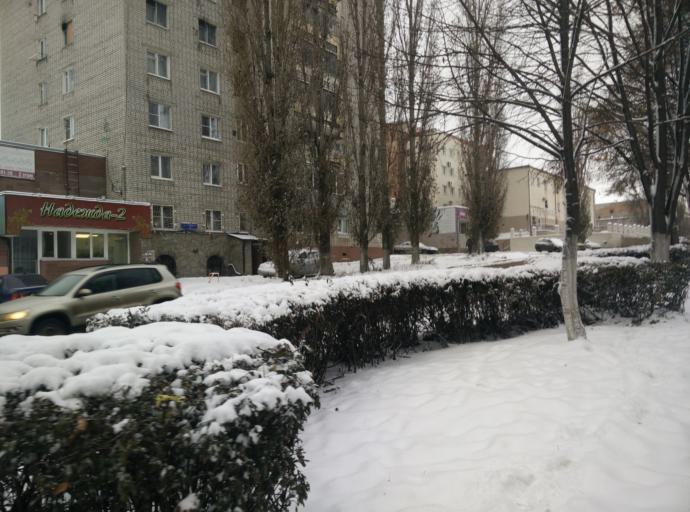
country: RU
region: Lipetsk
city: Lipetsk
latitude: 52.6069
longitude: 39.5824
